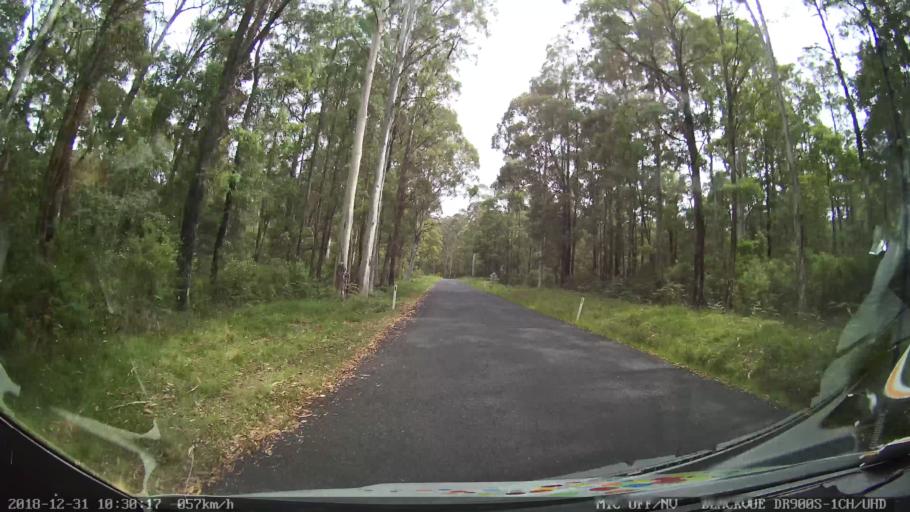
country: AU
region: New South Wales
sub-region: Snowy River
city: Jindabyne
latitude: -36.4645
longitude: 148.1510
